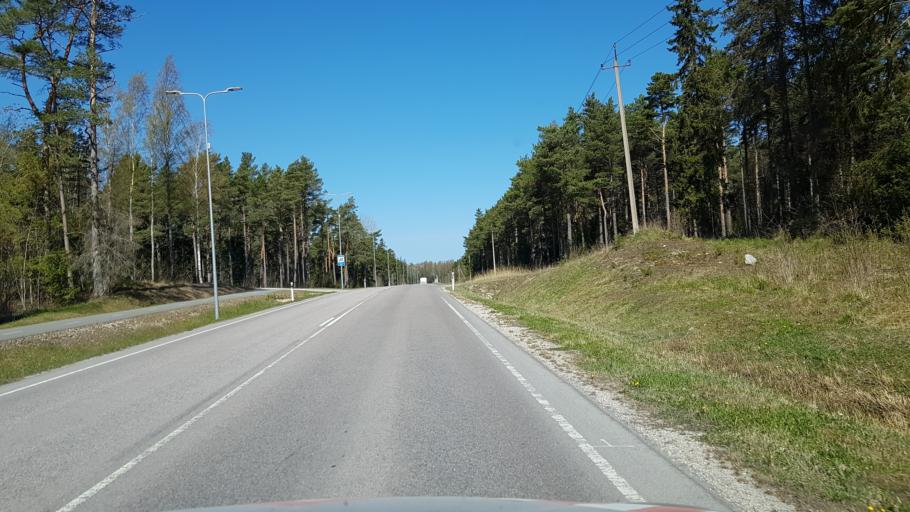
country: EE
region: Harju
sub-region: Viimsi vald
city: Viimsi
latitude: 59.5170
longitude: 24.9000
